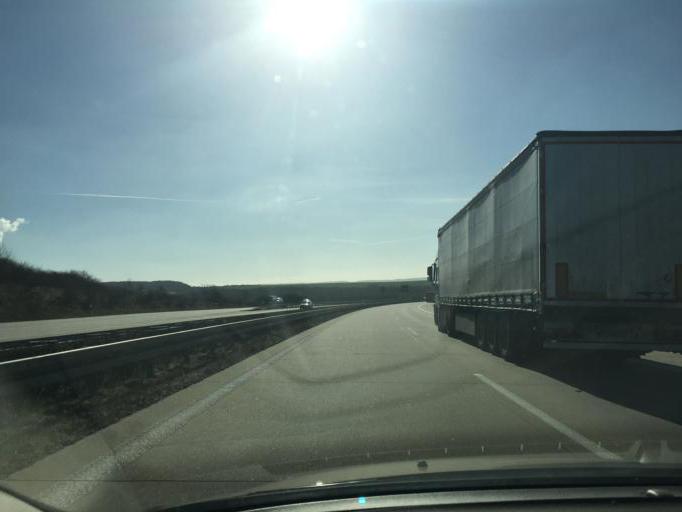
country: DE
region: Saxony
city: Wittgensdorf
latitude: 50.8539
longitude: 12.8365
